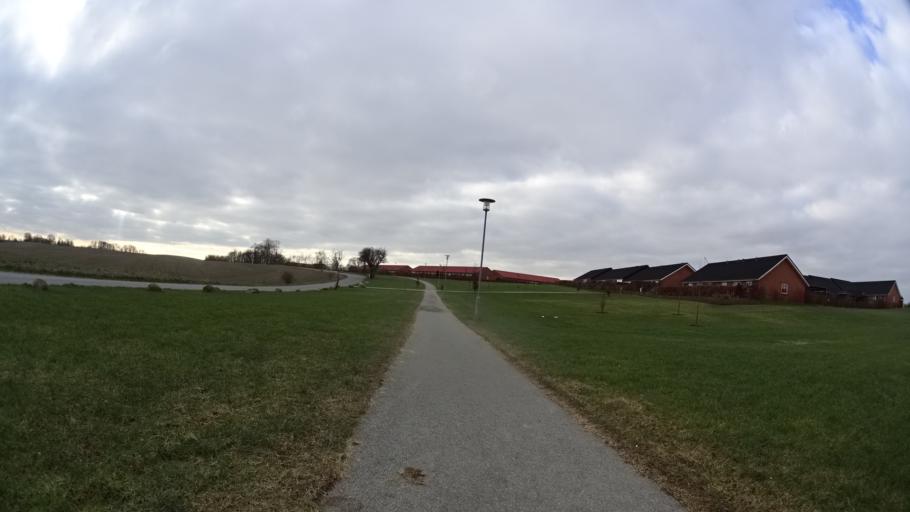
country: DK
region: Central Jutland
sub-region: Arhus Kommune
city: Tranbjerg
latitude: 56.0925
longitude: 10.1076
